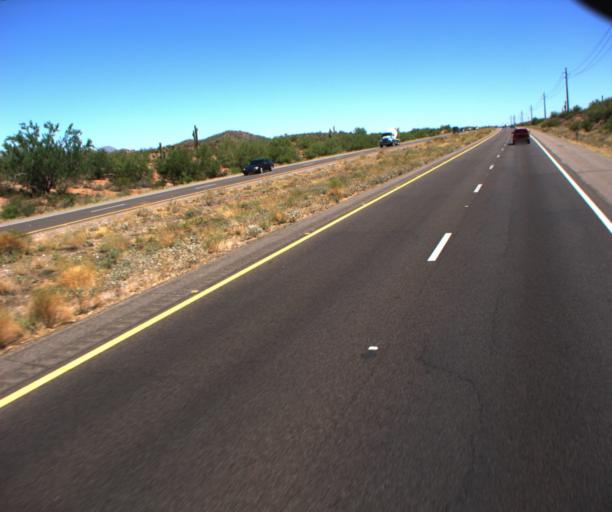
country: US
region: Arizona
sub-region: Maricopa County
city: Fountain Hills
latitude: 33.5400
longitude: -111.7245
